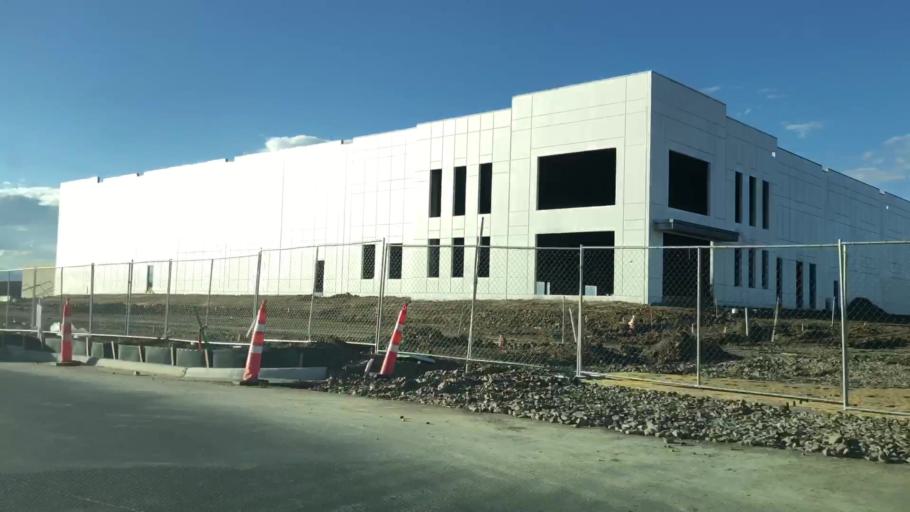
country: US
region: Colorado
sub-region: Larimer County
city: Loveland
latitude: 40.4304
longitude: -105.0096
